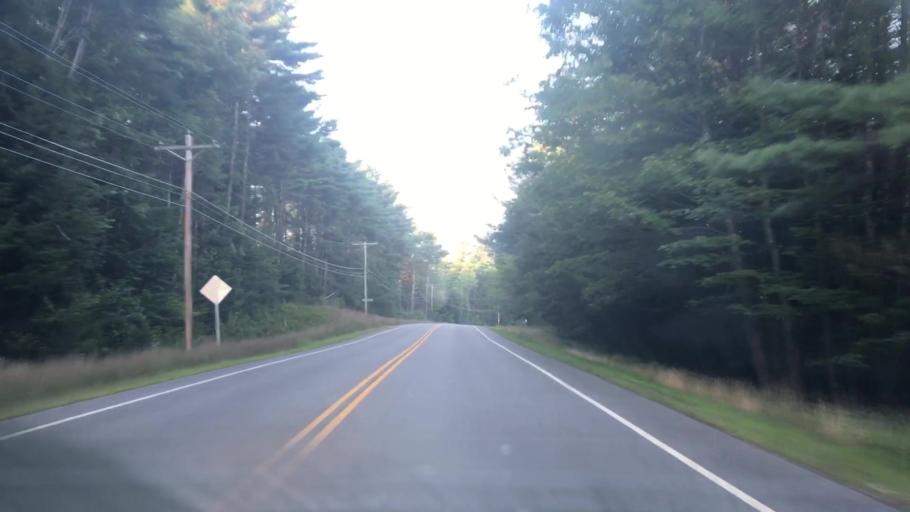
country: US
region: New Hampshire
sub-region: Belknap County
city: Gilmanton
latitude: 43.4278
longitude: -71.3507
